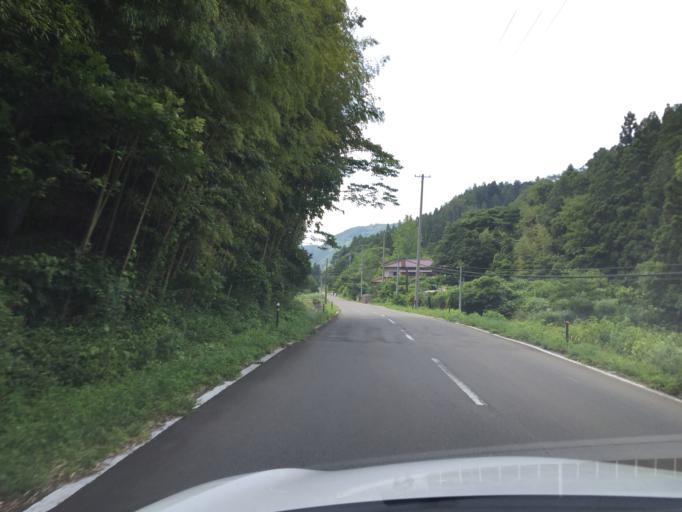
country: JP
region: Fukushima
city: Iwaki
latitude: 37.0549
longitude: 140.6933
